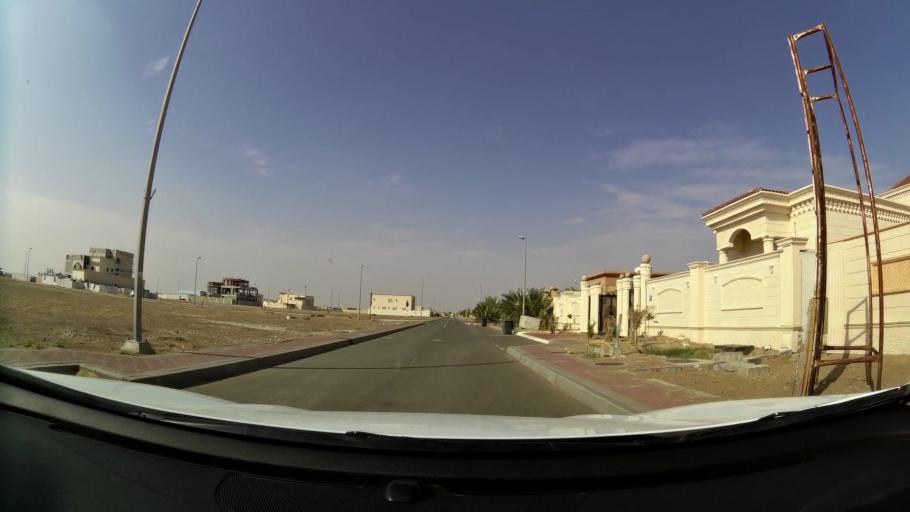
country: AE
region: Abu Dhabi
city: Al Ain
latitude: 24.0863
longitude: 55.8998
